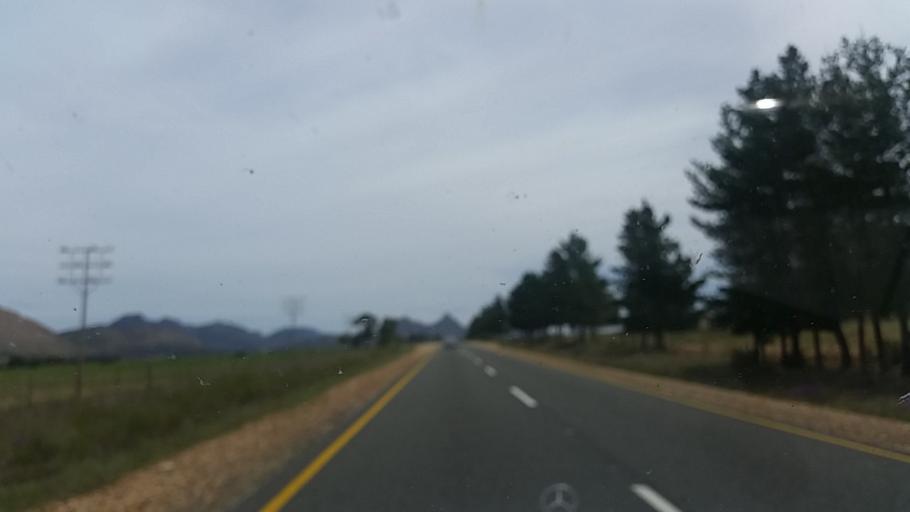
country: ZA
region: Western Cape
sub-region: Eden District Municipality
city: George
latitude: -33.8167
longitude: 22.5117
